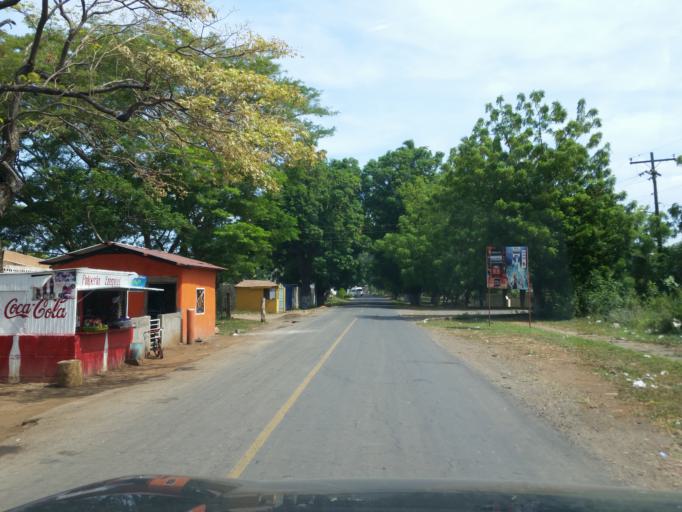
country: NI
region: Managua
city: Masachapa
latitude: 11.7960
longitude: -86.5161
